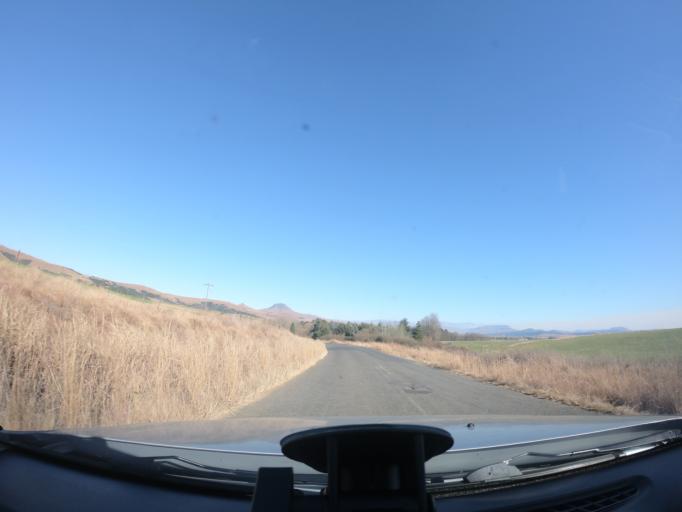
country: ZA
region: KwaZulu-Natal
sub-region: uMgungundlovu District Municipality
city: Mooirivier
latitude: -29.3271
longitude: 29.8511
